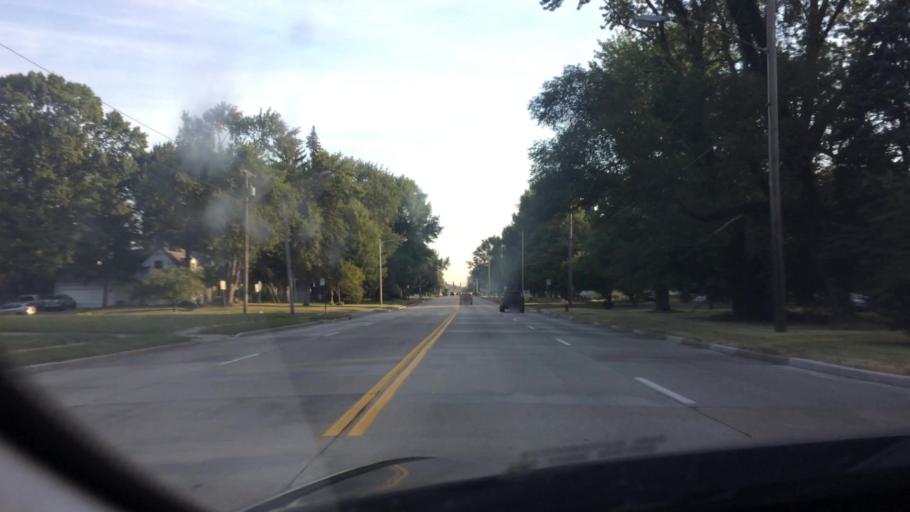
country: US
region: Ohio
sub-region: Lucas County
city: Ottawa Hills
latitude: 41.6835
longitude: -83.6442
